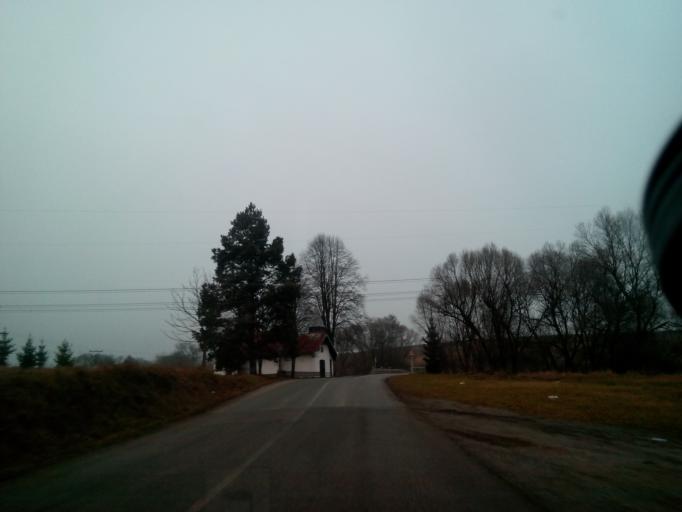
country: SK
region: Kosicky
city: Krompachy
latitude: 48.9577
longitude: 20.9533
